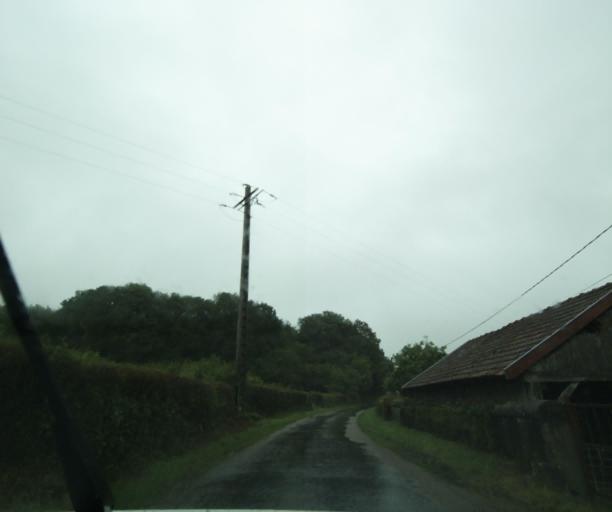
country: FR
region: Bourgogne
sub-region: Departement de Saone-et-Loire
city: Charolles
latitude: 46.4055
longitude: 4.2473
